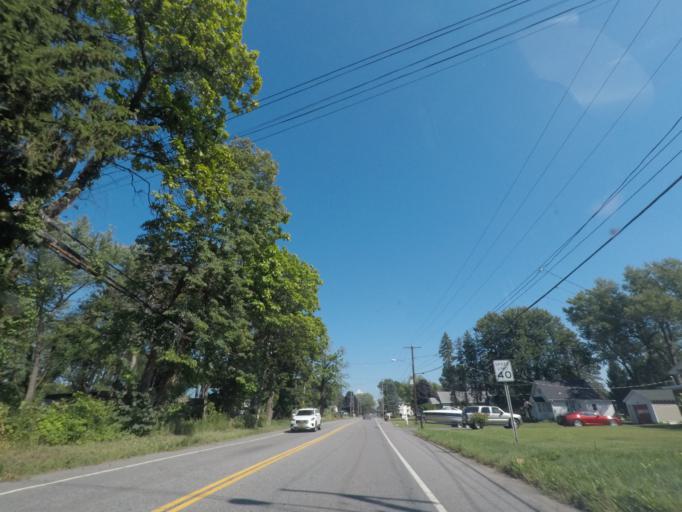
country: US
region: New York
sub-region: Albany County
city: Roessleville
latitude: 42.7388
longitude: -73.7895
